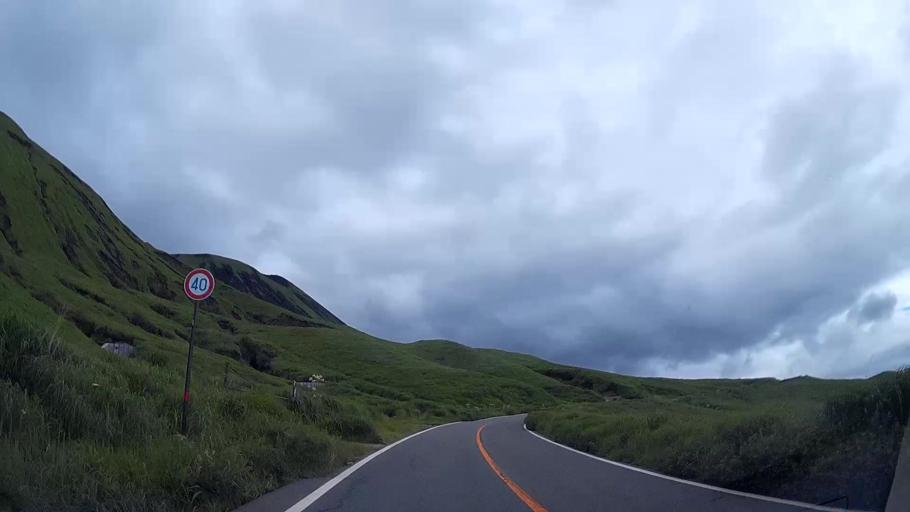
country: JP
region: Kumamoto
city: Aso
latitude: 32.9072
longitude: 131.0597
